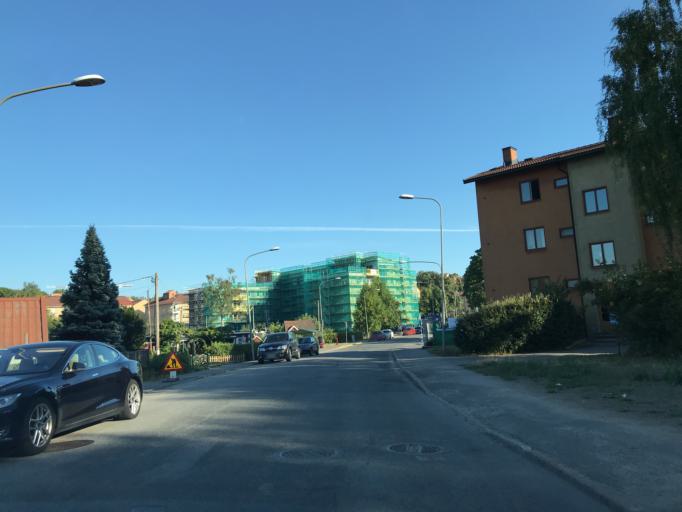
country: SE
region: Stockholm
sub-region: Stockholms Kommun
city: Bromma
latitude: 59.3396
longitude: 17.9522
